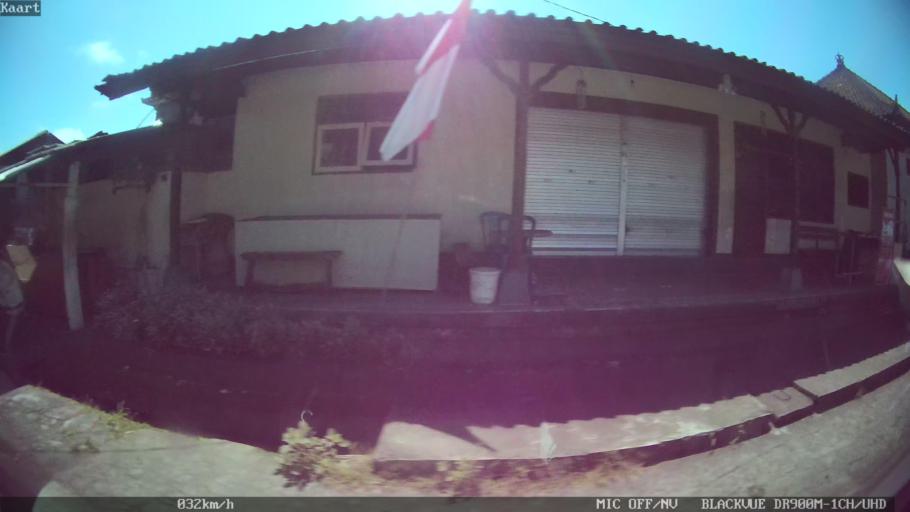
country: ID
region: Bali
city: Banjar Pasekan
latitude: -8.5764
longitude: 115.3235
